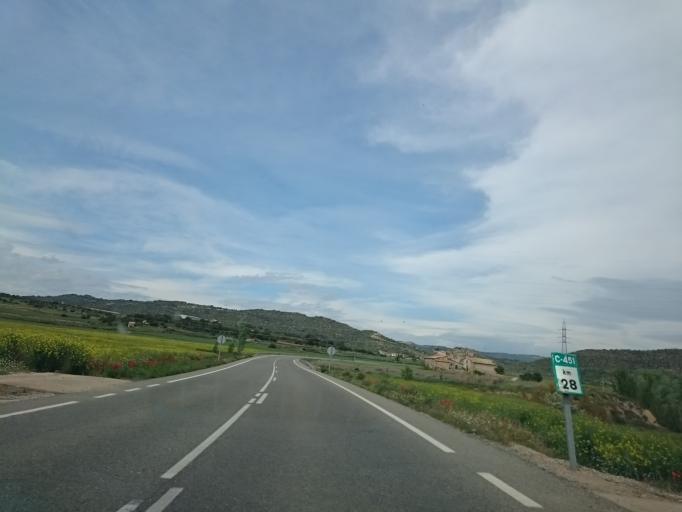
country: ES
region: Catalonia
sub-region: Provincia de Lleida
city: Tora de Riubregos
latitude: 41.8297
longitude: 1.3469
